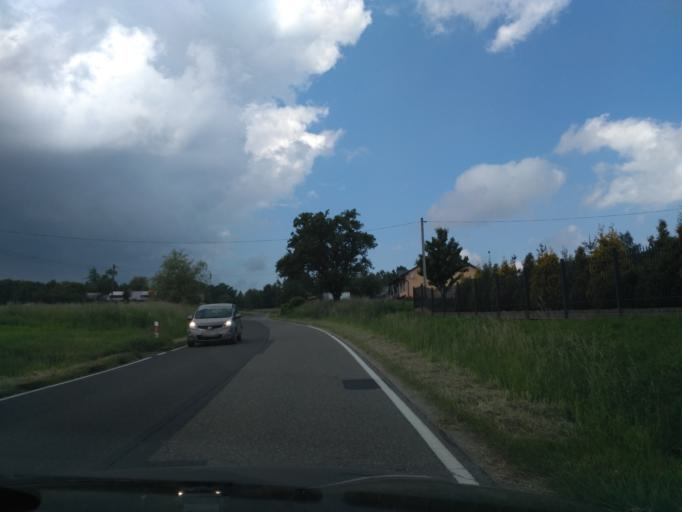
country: PL
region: Subcarpathian Voivodeship
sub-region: Powiat lancucki
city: Handzlowka
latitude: 49.9609
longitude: 22.1966
